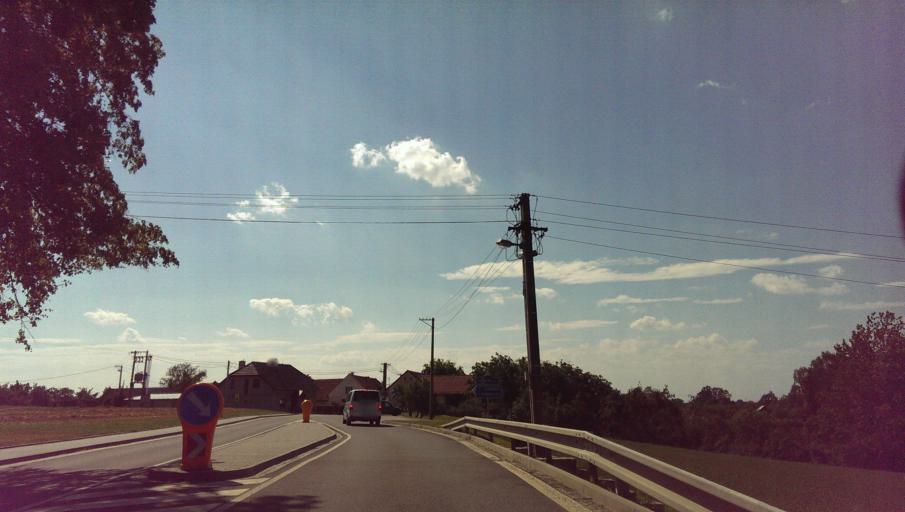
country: CZ
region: Zlin
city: Kelc
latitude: 49.4345
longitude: 17.7848
